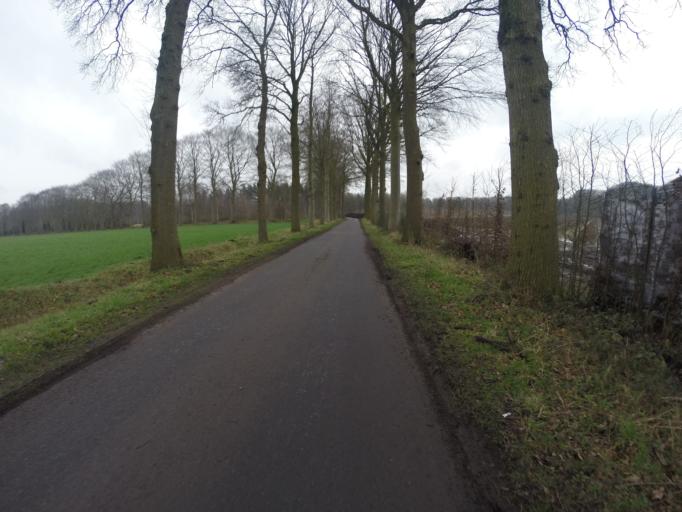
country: BE
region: Flanders
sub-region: Provincie West-Vlaanderen
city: Beernem
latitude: 51.1149
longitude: 3.3305
